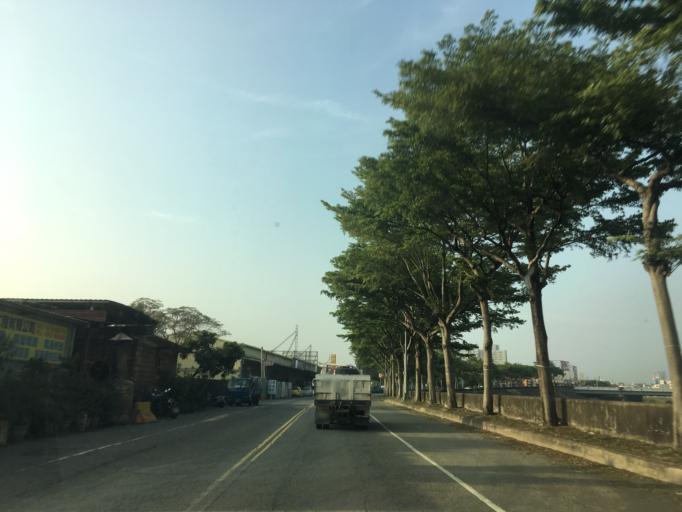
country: TW
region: Taiwan
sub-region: Taichung City
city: Taichung
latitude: 24.1618
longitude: 120.7036
